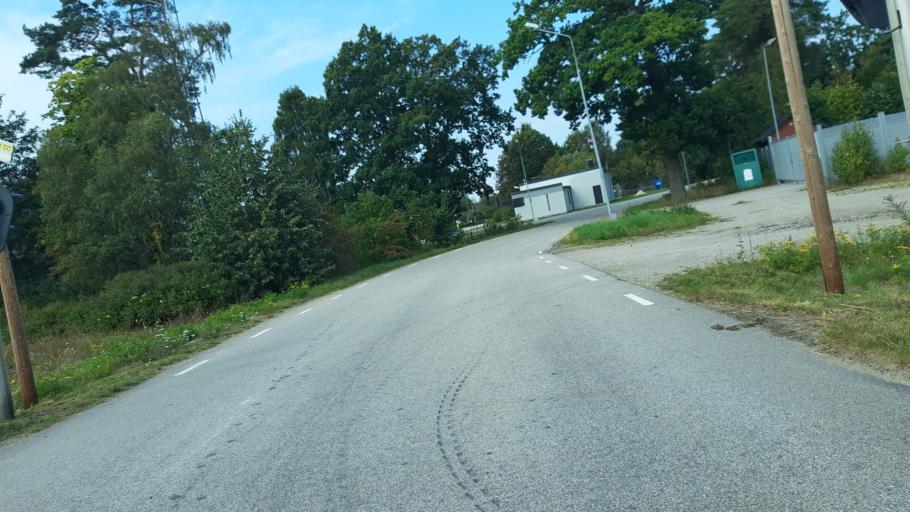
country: SE
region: Blekinge
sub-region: Karlskrona Kommun
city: Nattraby
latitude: 56.2269
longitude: 15.4220
